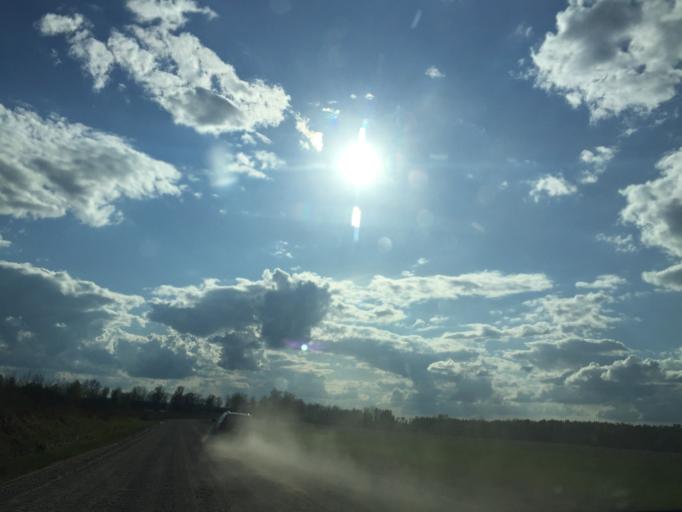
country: LV
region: Beverina
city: Murmuiza
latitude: 57.4009
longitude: 25.5052
